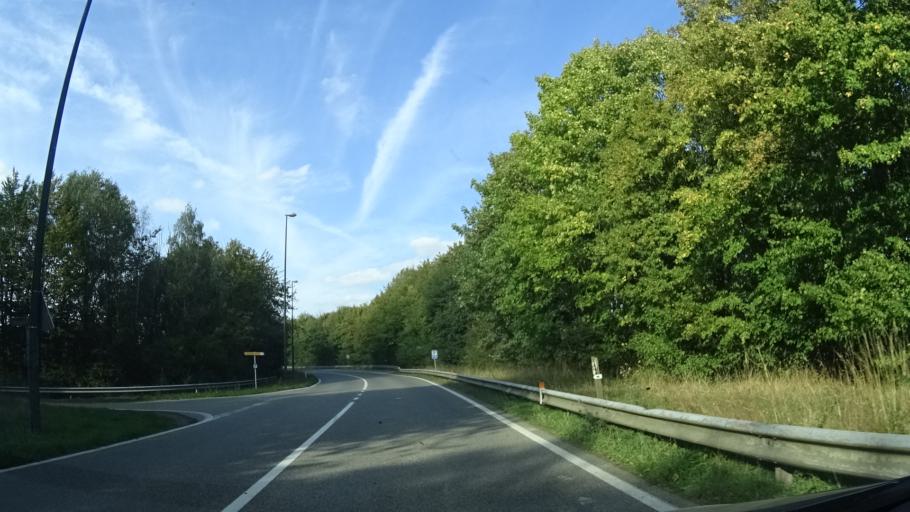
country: BE
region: Wallonia
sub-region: Province de Namur
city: Cerfontaine
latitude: 50.2189
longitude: 4.3829
